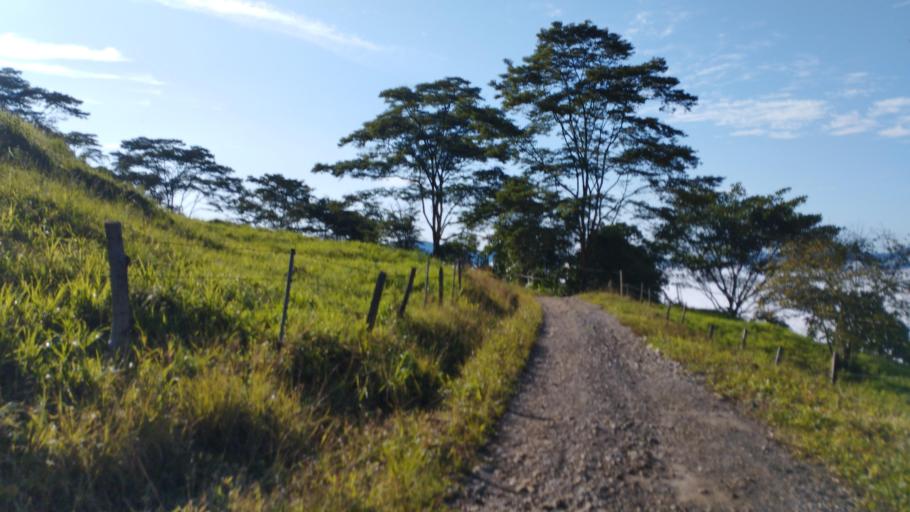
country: CO
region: Boyaca
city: San Luis de Gaceno
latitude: 4.7893
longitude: -73.0967
